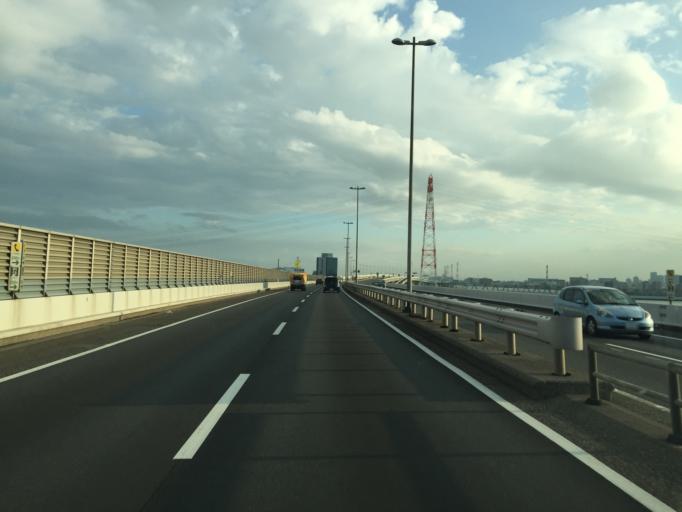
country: JP
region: Tokyo
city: Urayasu
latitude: 35.6921
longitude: 139.8591
